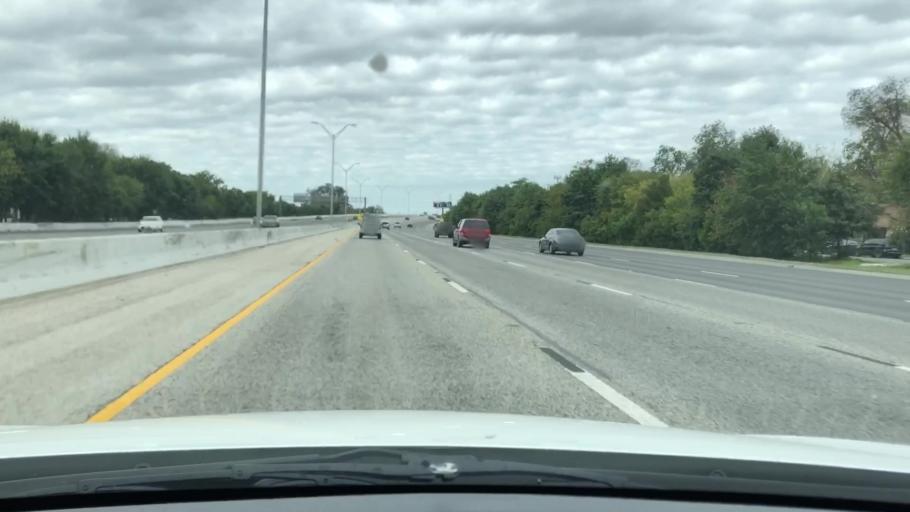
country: US
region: Texas
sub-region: Bexar County
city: San Antonio
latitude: 29.3968
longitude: -98.5223
